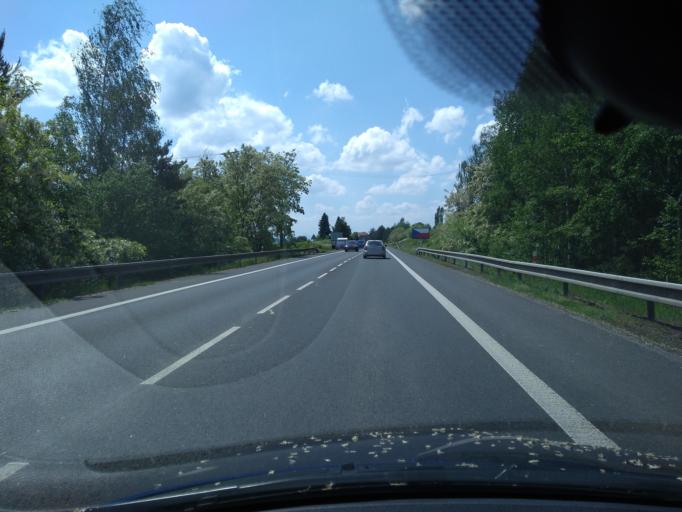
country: CZ
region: Plzensky
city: Svihov
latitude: 49.5068
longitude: 13.2976
